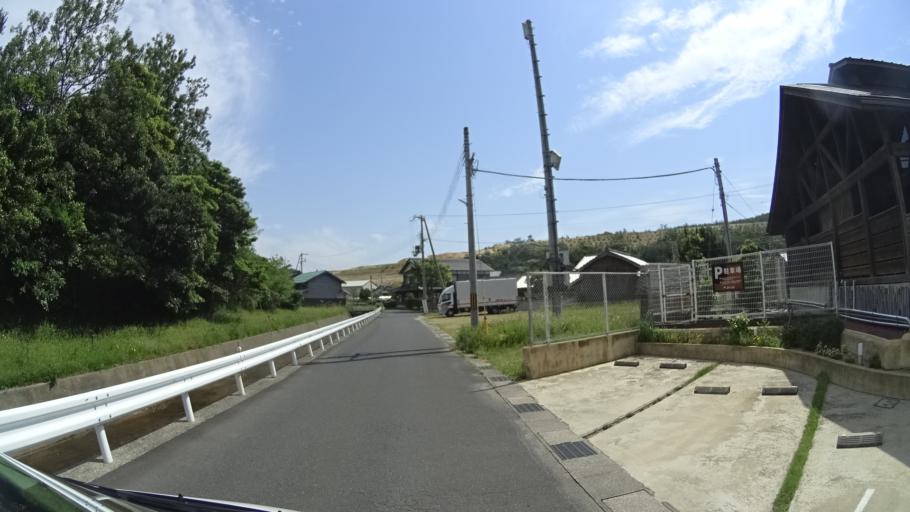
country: JP
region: Kyoto
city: Miyazu
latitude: 35.7011
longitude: 135.0542
